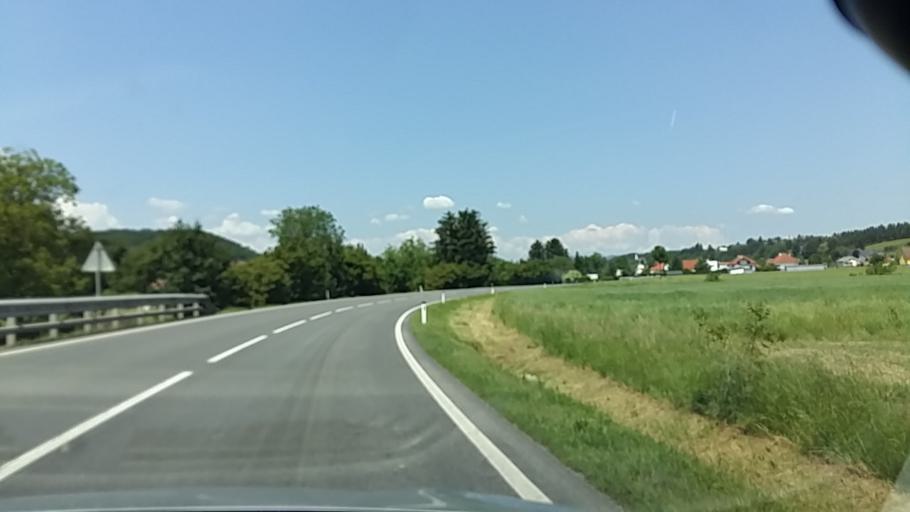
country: AT
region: Burgenland
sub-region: Politischer Bezirk Oberpullendorf
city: Oberpullendorf
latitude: 47.4815
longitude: 16.4861
